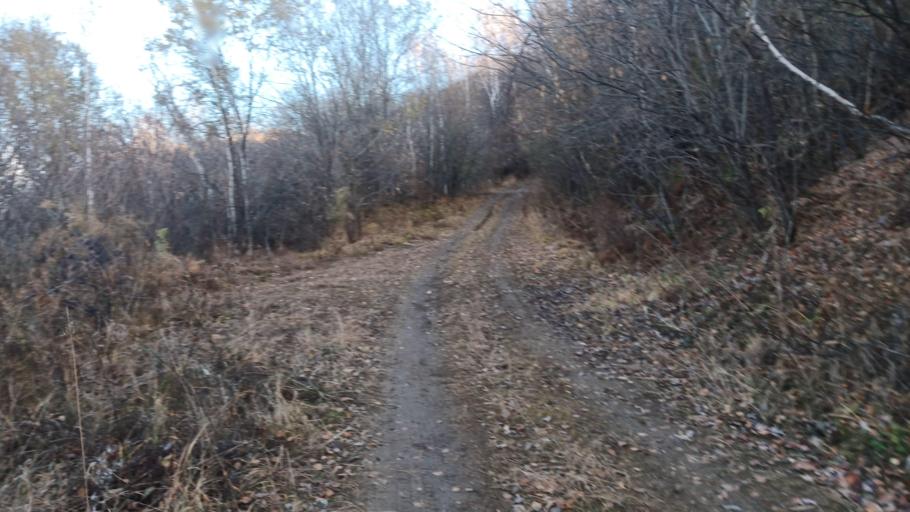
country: RU
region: Altai Krai
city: Gon'ba
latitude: 53.4343
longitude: 83.5523
